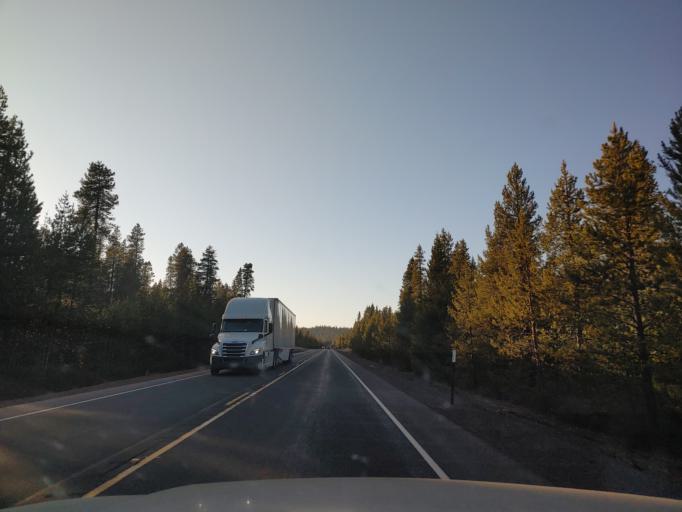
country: US
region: Oregon
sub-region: Deschutes County
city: La Pine
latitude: 43.4326
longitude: -121.8557
